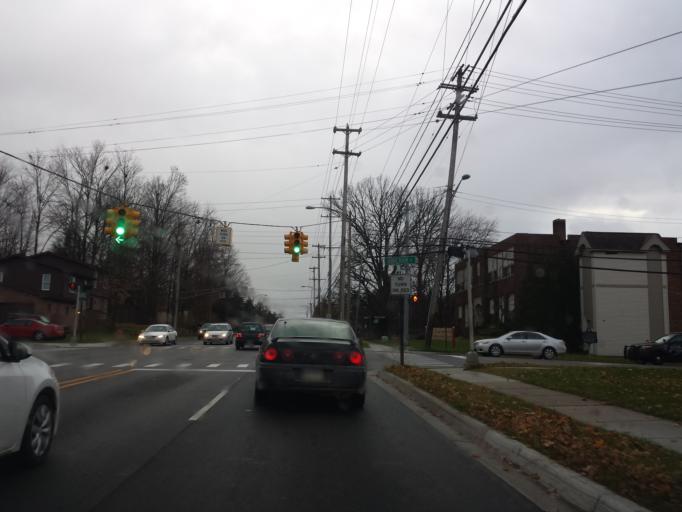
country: US
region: Michigan
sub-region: Ingham County
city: East Lansing
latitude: 42.7409
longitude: -84.4623
